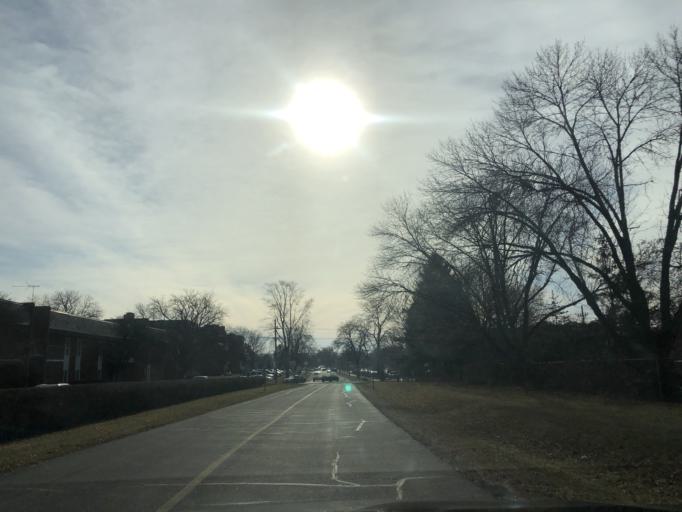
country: US
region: Illinois
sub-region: DuPage County
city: Downers Grove
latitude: 41.8121
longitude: -88.0149
